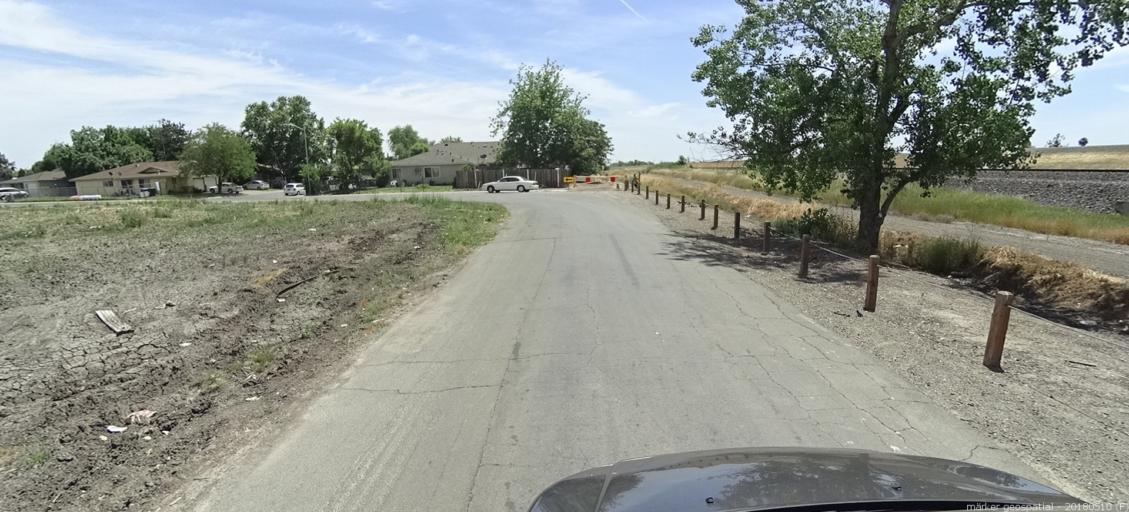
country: US
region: California
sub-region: Sacramento County
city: Sacramento
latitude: 38.6291
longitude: -121.4689
